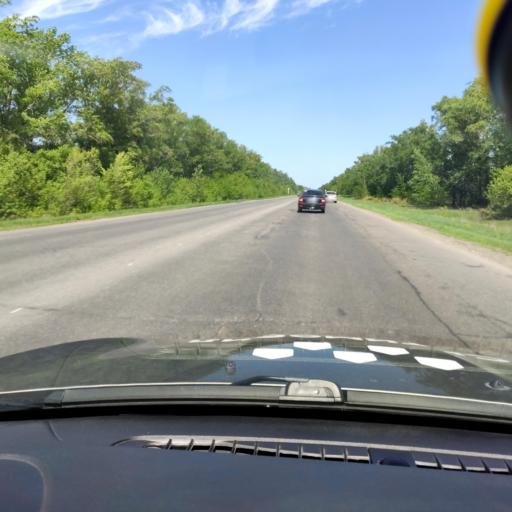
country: RU
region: Samara
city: Tol'yatti
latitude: 53.5988
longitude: 49.4086
